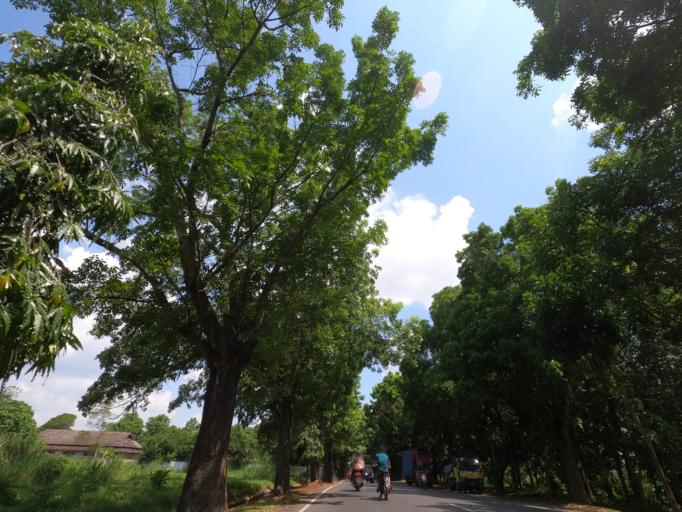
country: ID
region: West Java
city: Pamanukan
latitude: -6.5515
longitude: 107.7413
